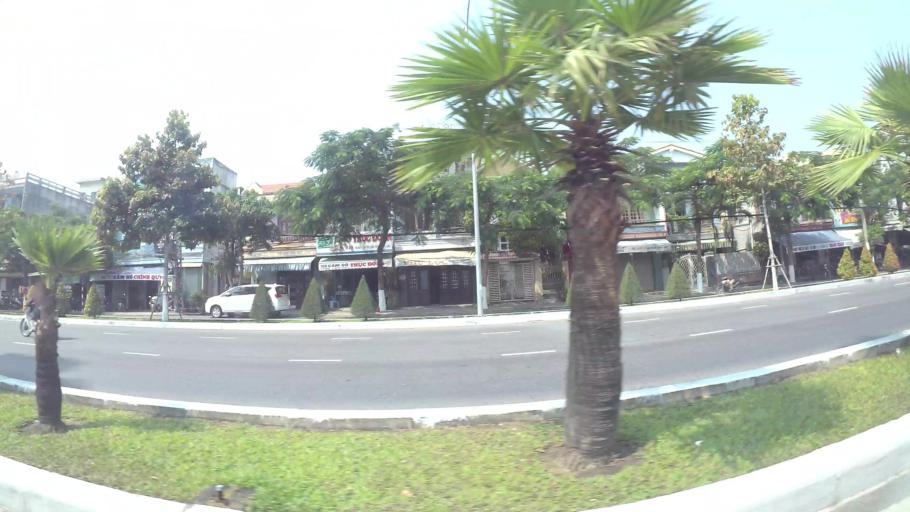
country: VN
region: Da Nang
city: Son Tra
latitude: 16.0464
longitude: 108.2390
